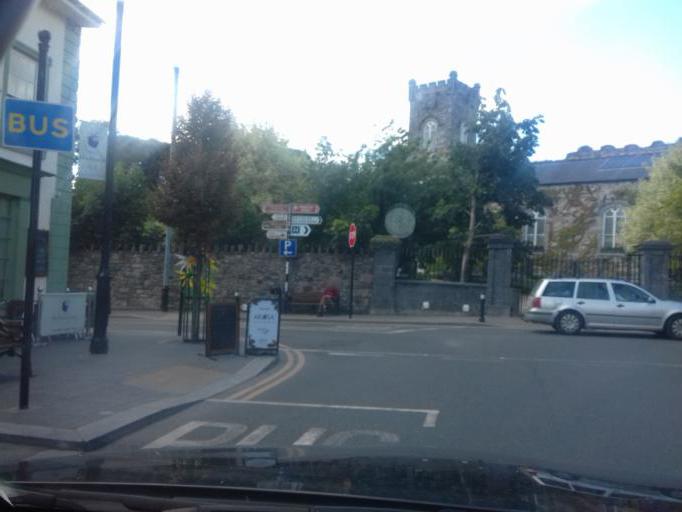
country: IE
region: Leinster
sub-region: Kilkenny
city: Thomastown
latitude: 52.5256
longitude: -7.1389
